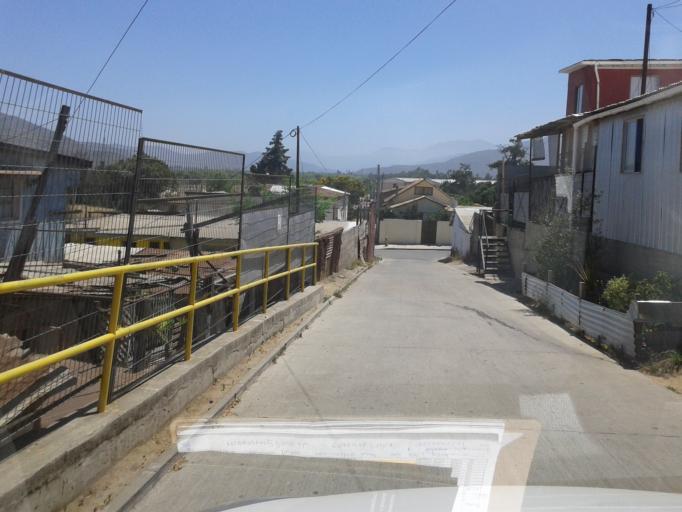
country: CL
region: Valparaiso
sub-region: Provincia de Quillota
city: Quillota
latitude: -32.8721
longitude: -71.2464
